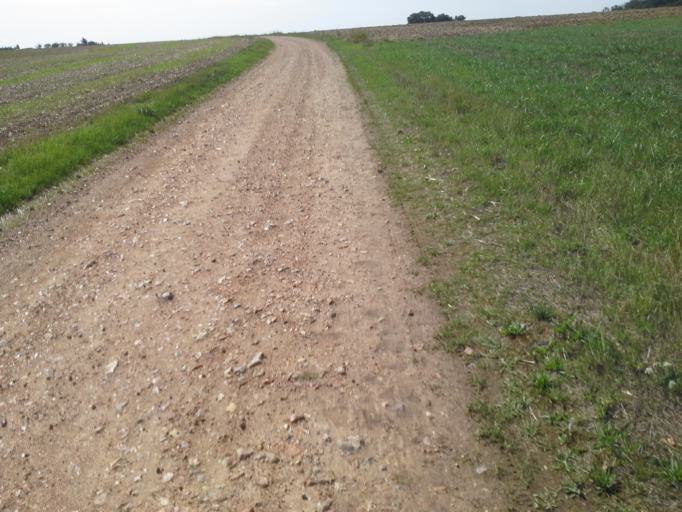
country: FR
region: Centre
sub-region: Departement du Loir-et-Cher
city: Villiers-sur-Loir
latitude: 47.8201
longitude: 0.9897
